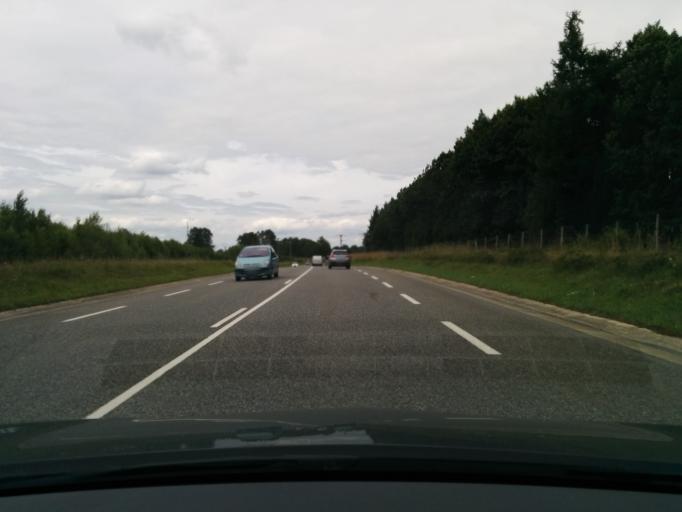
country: FR
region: Midi-Pyrenees
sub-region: Departement des Hautes-Pyrenees
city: La Barthe-de-Neste
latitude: 43.0740
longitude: 0.3618
